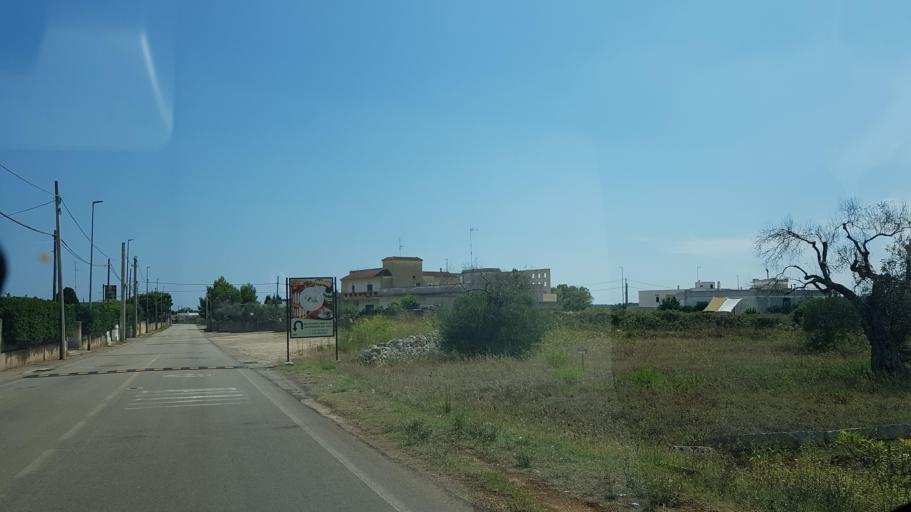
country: IT
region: Apulia
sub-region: Provincia di Lecce
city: Castrignano del Capo
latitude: 39.8279
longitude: 18.3524
